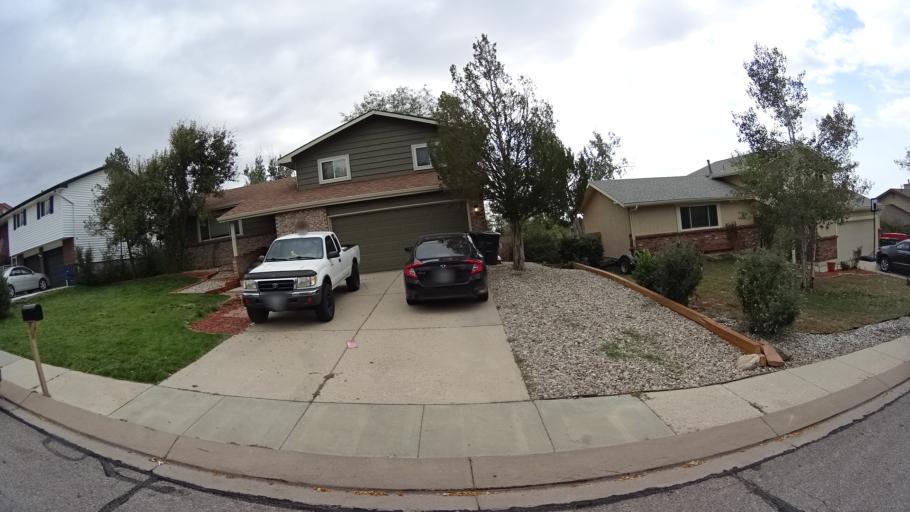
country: US
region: Colorado
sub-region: El Paso County
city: Cimarron Hills
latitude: 38.8865
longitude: -104.7293
